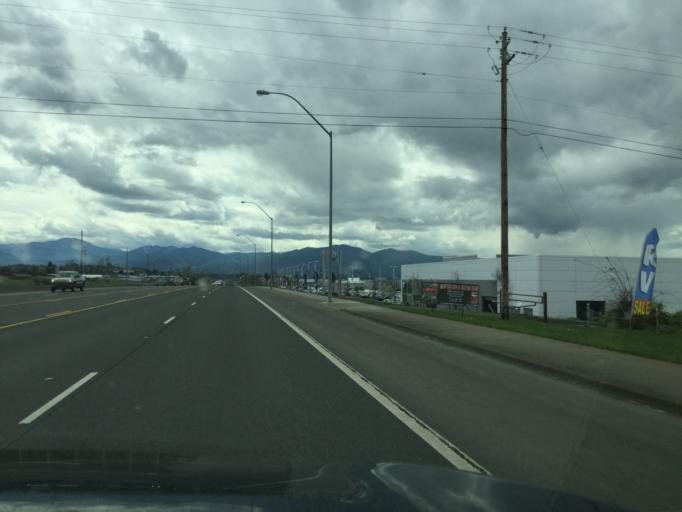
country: US
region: Oregon
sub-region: Jackson County
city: White City
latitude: 42.3826
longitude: -122.8561
